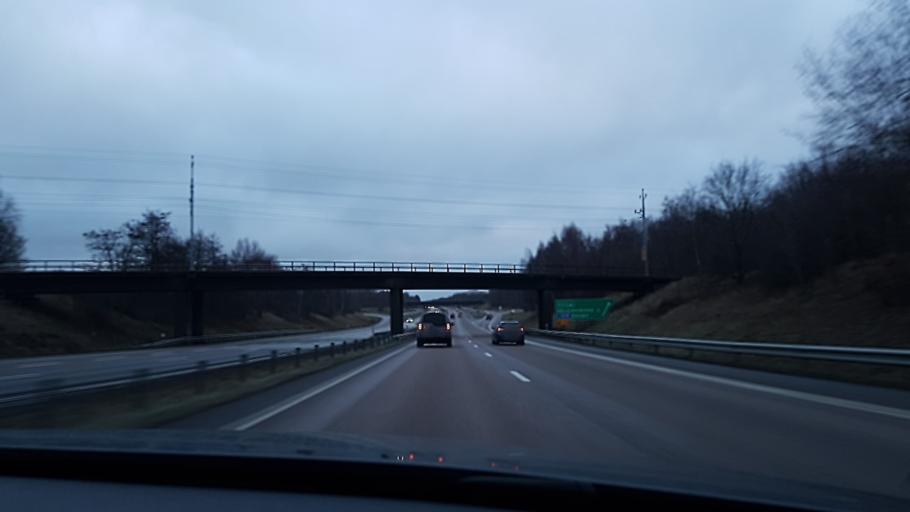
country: SE
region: Skane
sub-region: Helsingborg
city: Barslov
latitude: 56.0240
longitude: 12.7835
